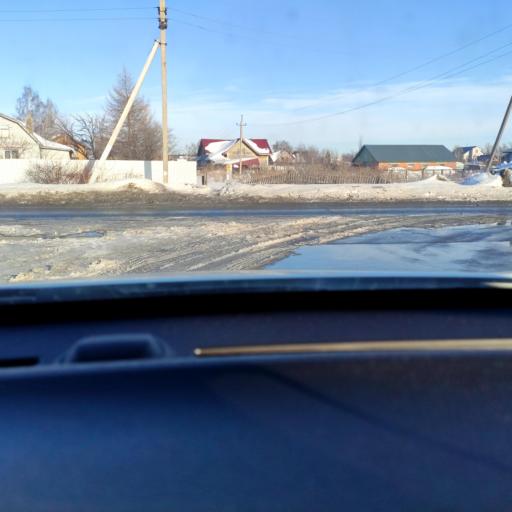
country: RU
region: Tatarstan
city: Osinovo
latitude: 55.8634
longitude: 48.8362
